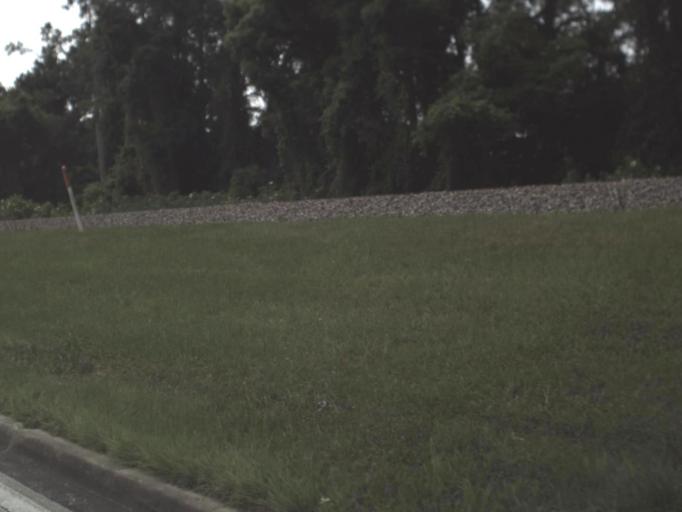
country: US
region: Florida
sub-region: Duval County
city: Jacksonville
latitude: 30.2614
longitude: -81.7028
